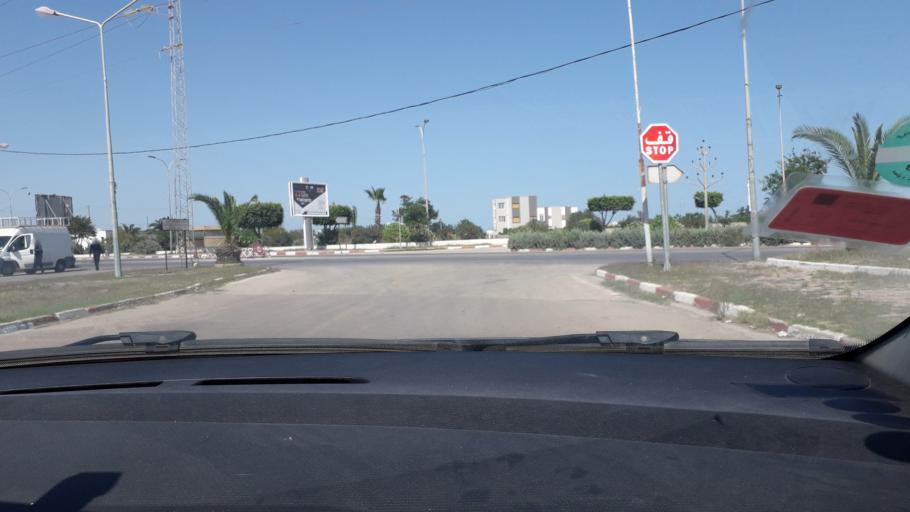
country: TN
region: Safaqis
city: Al Qarmadah
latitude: 34.8364
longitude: 10.7646
